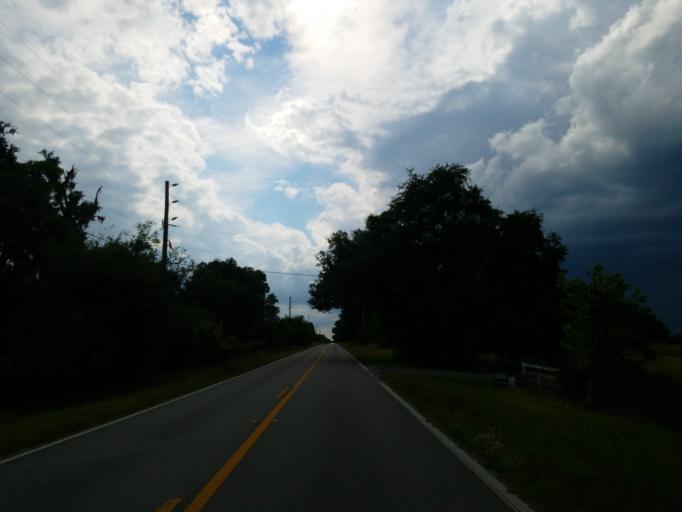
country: US
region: Florida
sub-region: Hernando County
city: Hill 'n Dale
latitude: 28.5533
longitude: -82.3327
